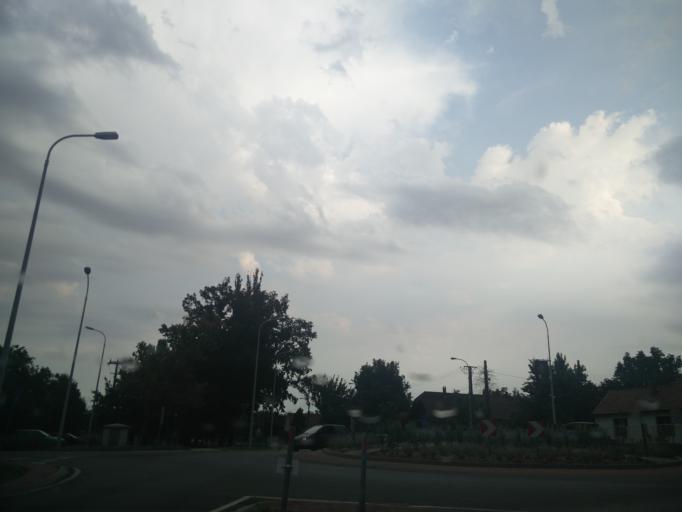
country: HU
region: Fejer
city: Velence
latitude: 47.2264
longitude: 18.6659
